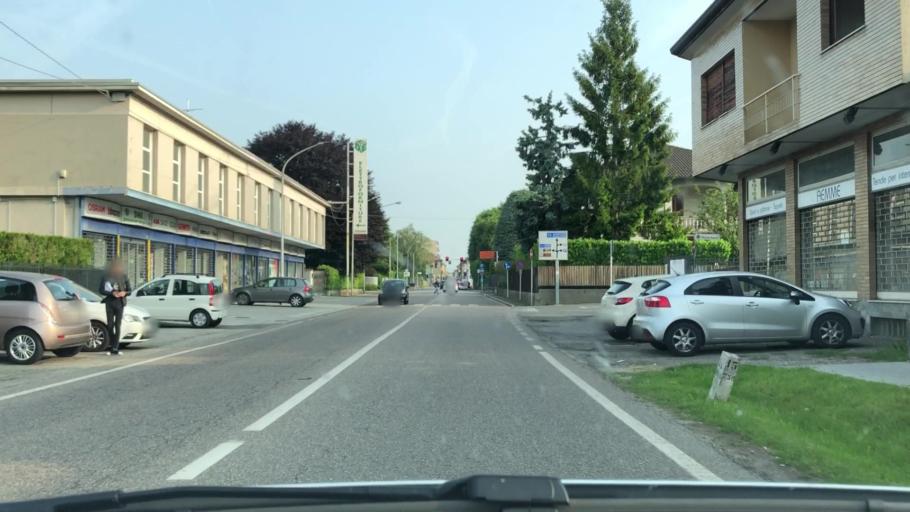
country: IT
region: Lombardy
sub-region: Provincia di Monza e Brianza
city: Barlassina
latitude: 45.6527
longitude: 9.1313
